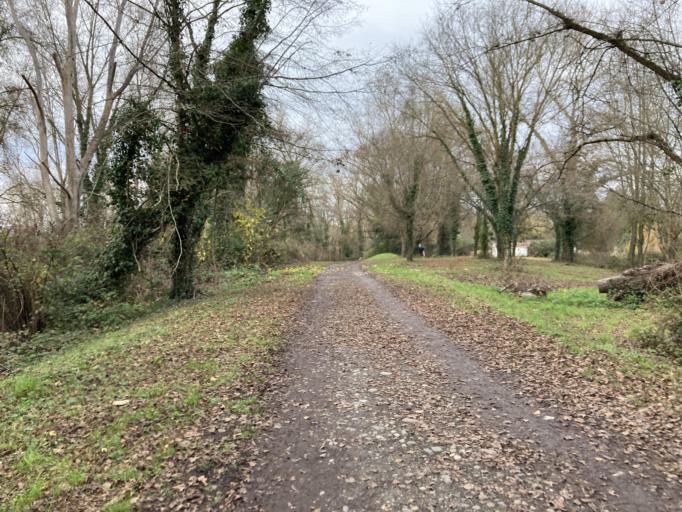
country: FR
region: Aquitaine
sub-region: Departement des Pyrenees-Atlantiques
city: Artiguelouve
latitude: 43.3125
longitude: -0.4490
